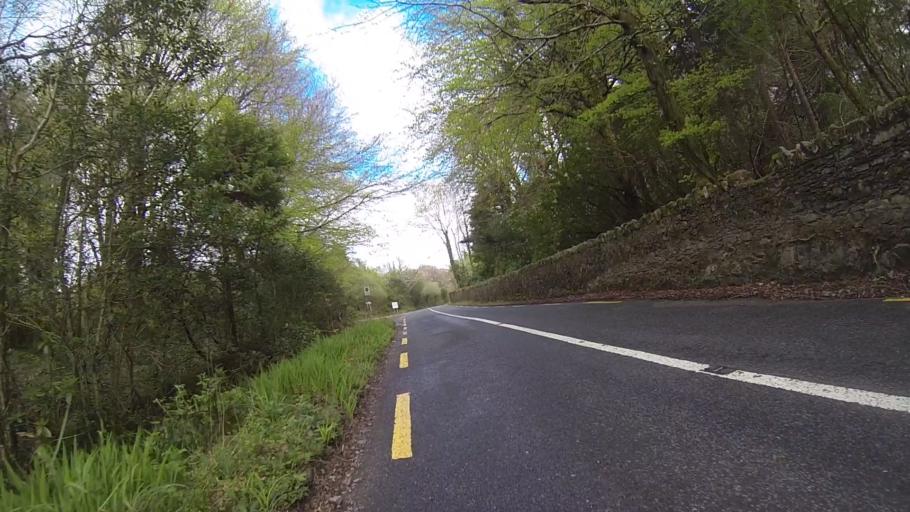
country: IE
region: Munster
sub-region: Ciarrai
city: Kenmare
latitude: 51.8202
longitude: -9.8644
